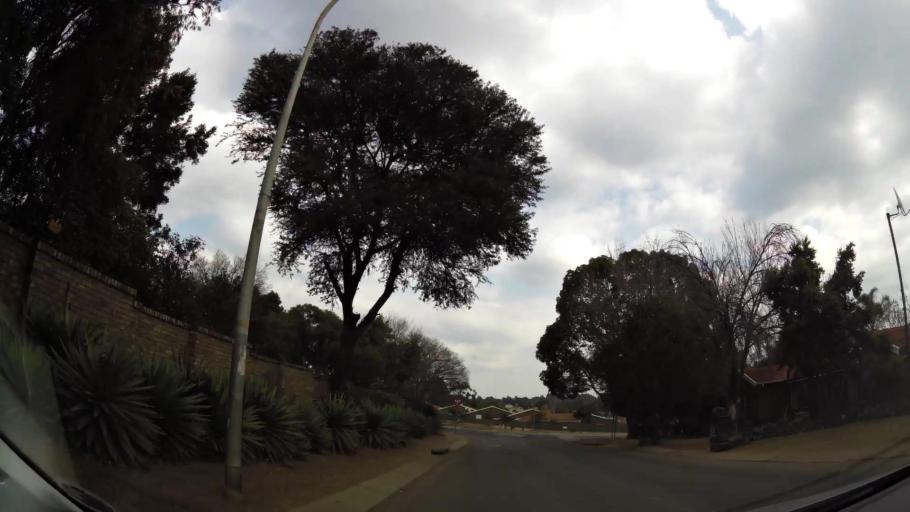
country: ZA
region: Gauteng
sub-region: City of Tshwane Metropolitan Municipality
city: Pretoria
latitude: -25.7625
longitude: 28.3115
